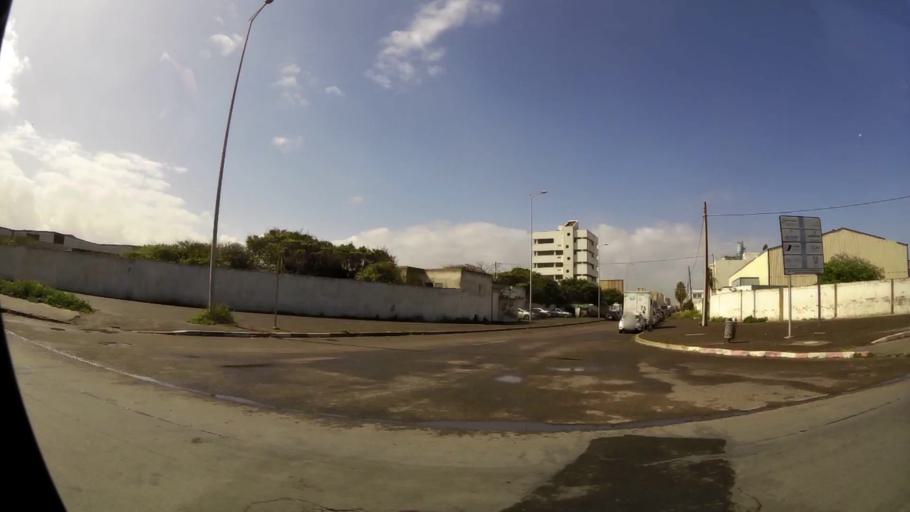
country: MA
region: Grand Casablanca
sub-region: Mediouna
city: Tit Mellil
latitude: 33.6272
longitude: -7.5145
